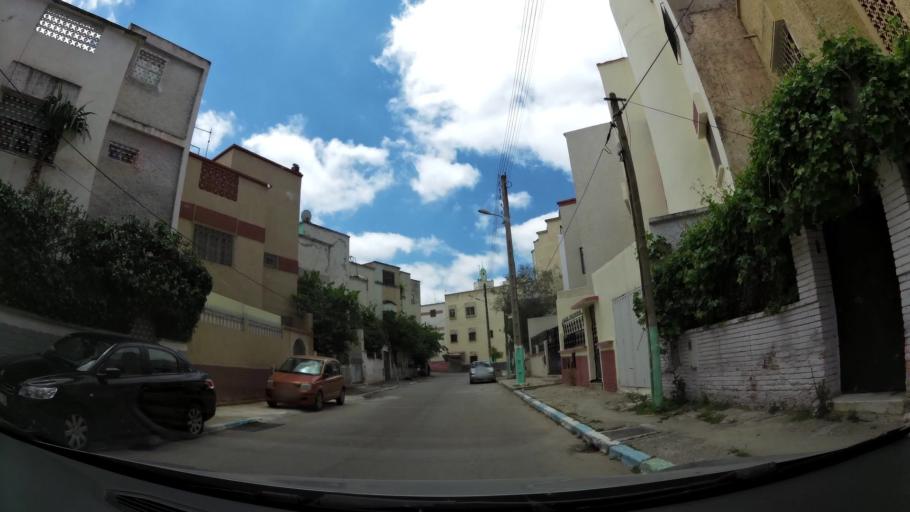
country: MA
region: Fes-Boulemane
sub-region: Fes
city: Fes
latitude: 34.0385
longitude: -5.0205
